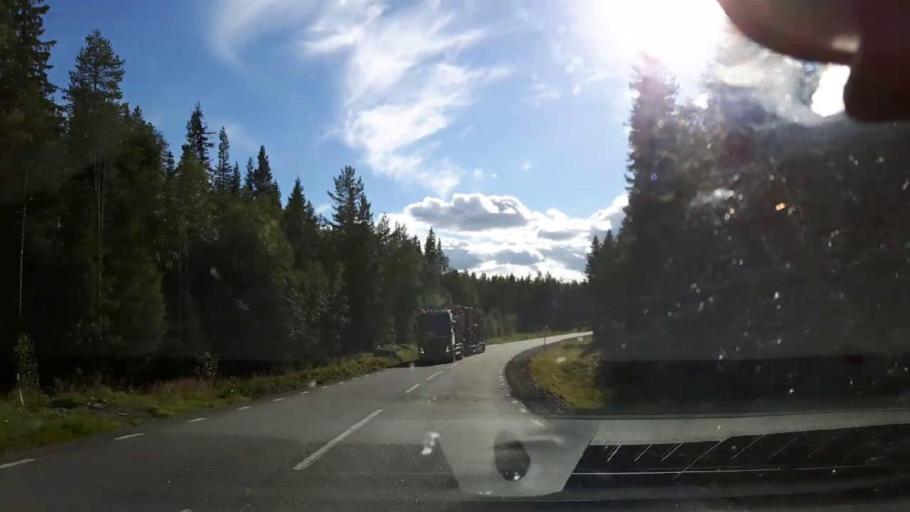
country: SE
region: Jaemtland
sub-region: Ragunda Kommun
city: Hammarstrand
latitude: 63.5346
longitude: 16.0678
